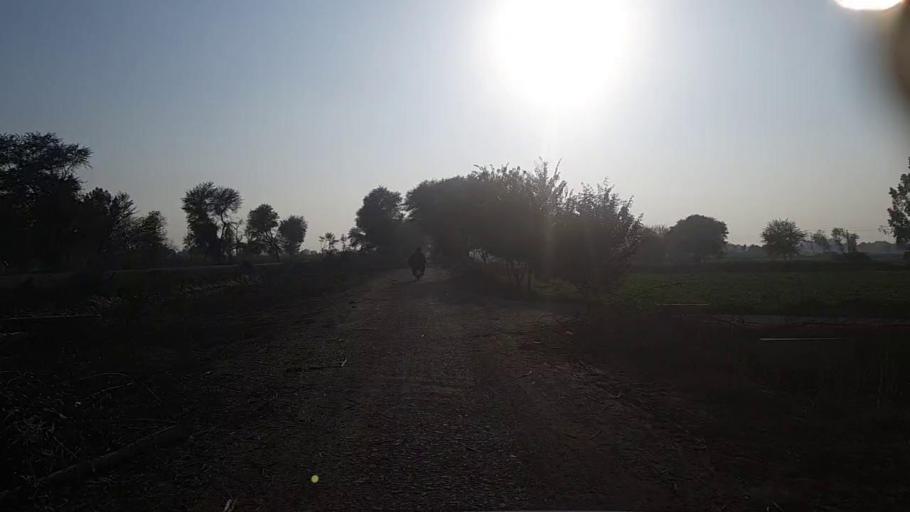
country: PK
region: Sindh
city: Khairpur
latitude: 28.0754
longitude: 69.7361
